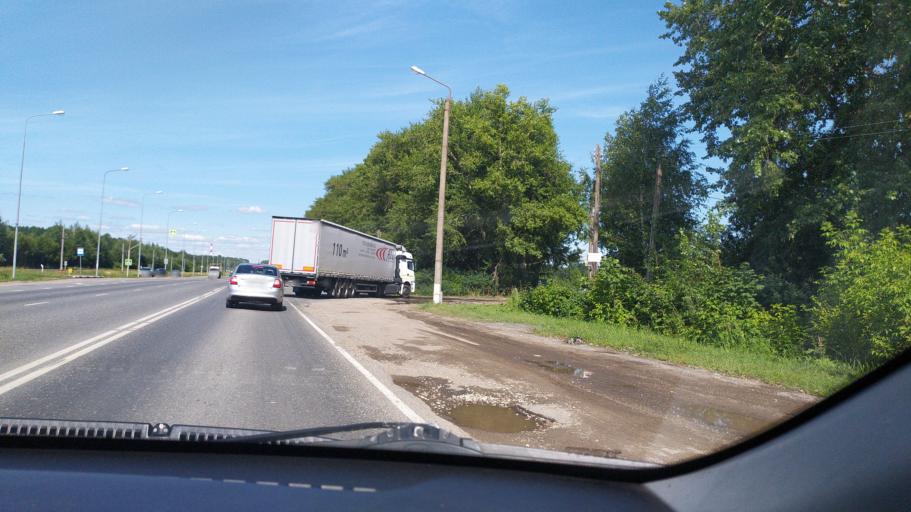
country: RU
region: Chuvashia
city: Novyye Lapsary
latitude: 56.0805
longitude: 47.2309
